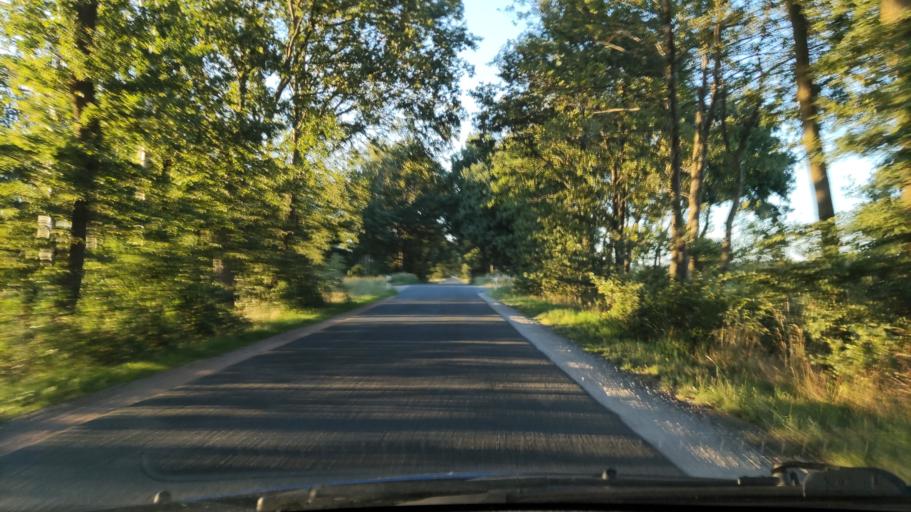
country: DE
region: Lower Saxony
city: Klein Gusborn
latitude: 53.0720
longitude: 11.1907
